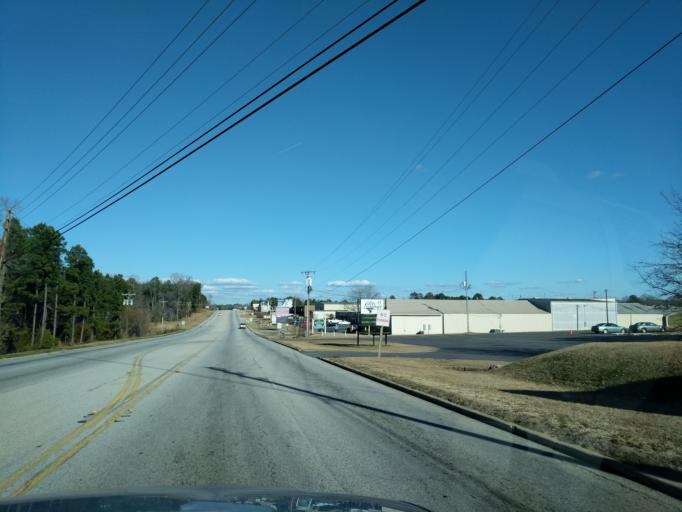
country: US
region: South Carolina
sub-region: Greenwood County
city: Greenwood
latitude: 34.2234
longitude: -82.1181
